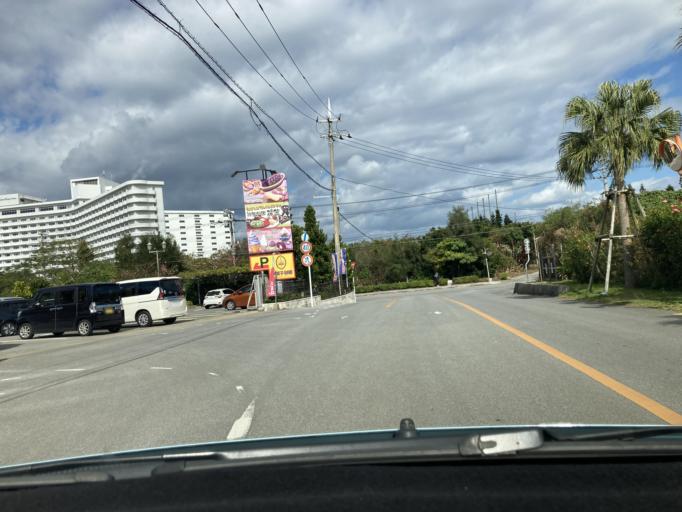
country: JP
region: Okinawa
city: Ishikawa
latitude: 26.4328
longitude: 127.7194
